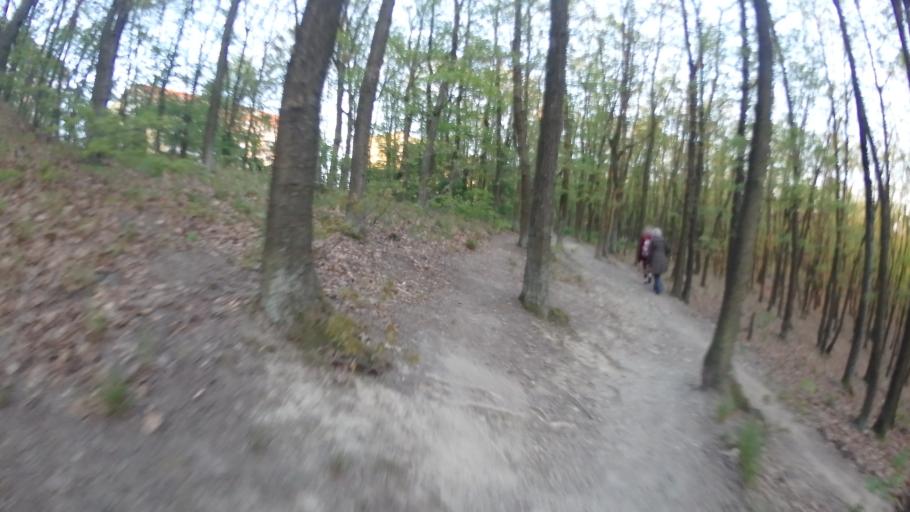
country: CZ
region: South Moravian
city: Troubsko
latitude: 49.1883
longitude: 16.5311
